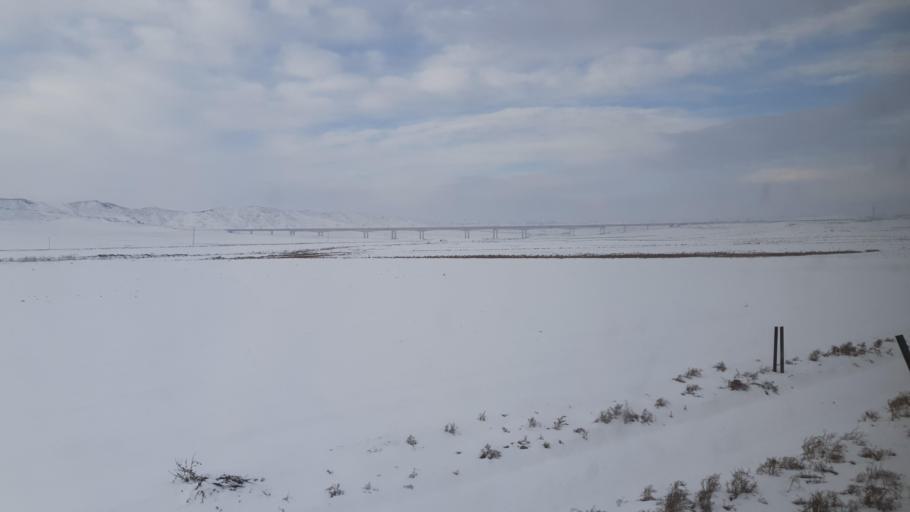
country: TR
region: Kirikkale
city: Delice
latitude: 39.8930
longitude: 33.9913
